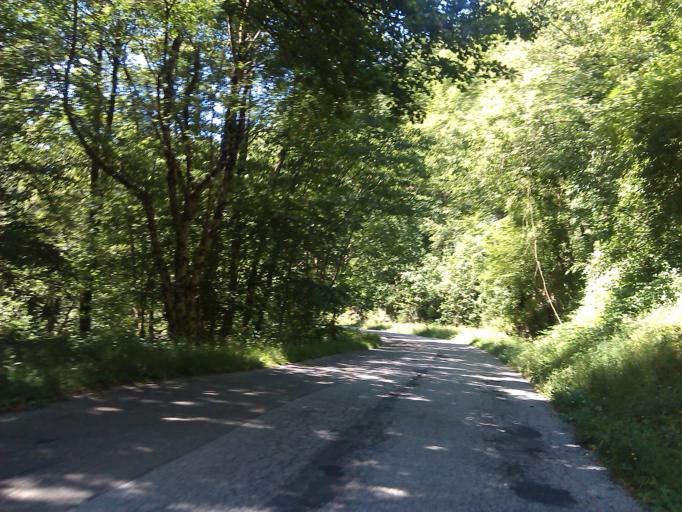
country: IT
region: Tuscany
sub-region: Provincia di Prato
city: Cantagallo
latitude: 44.0616
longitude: 11.0496
